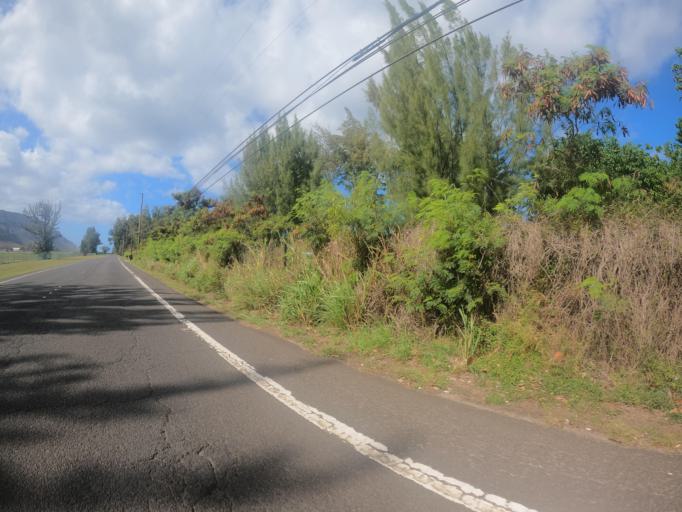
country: US
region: Hawaii
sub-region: Honolulu County
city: Mokuleia
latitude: 21.5811
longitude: -158.1992
